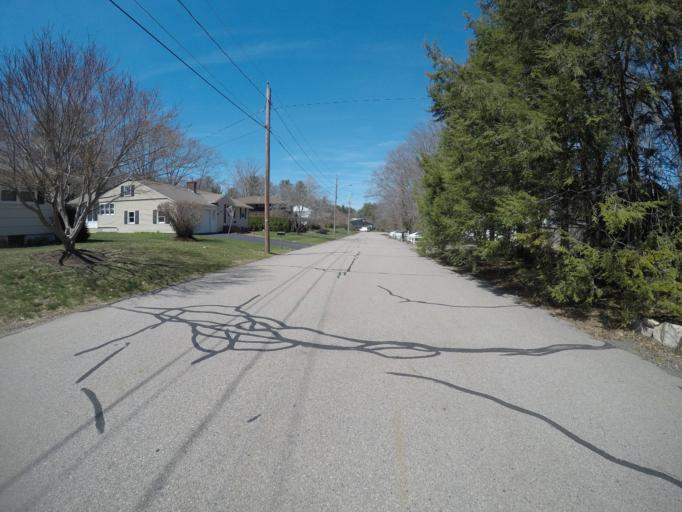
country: US
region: Massachusetts
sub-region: Bristol County
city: Easton
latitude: 42.0470
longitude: -71.0877
